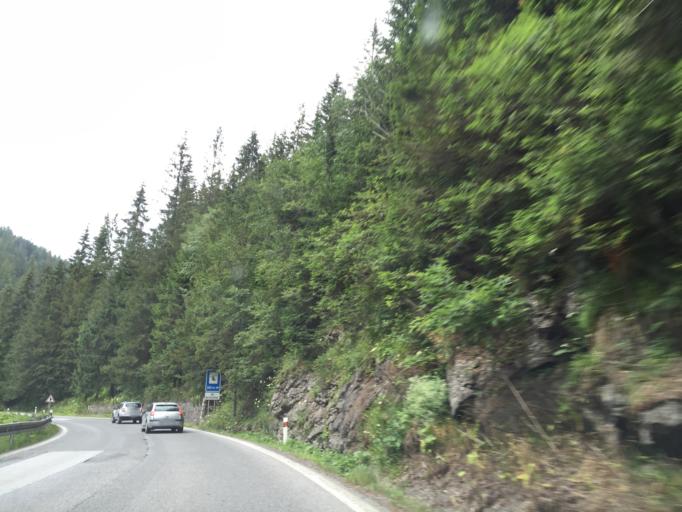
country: SK
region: Presovsky
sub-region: Okres Poprad
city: Zdiar
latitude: 49.2620
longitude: 20.3009
